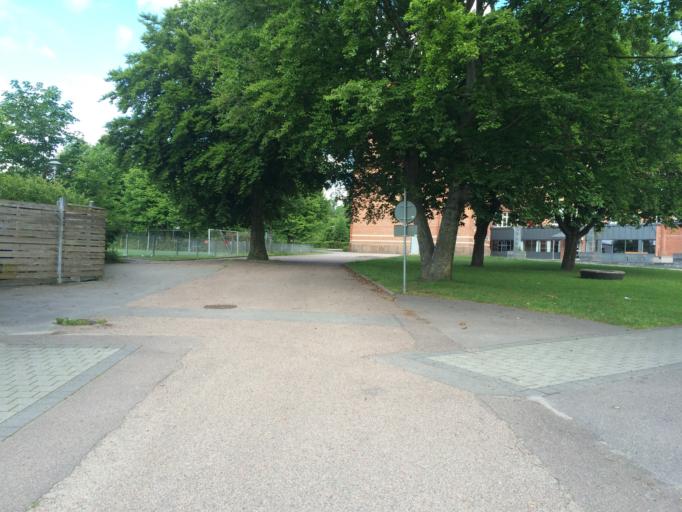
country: SE
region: Halland
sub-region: Halmstads Kommun
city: Halmstad
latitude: 56.6722
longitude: 12.8451
